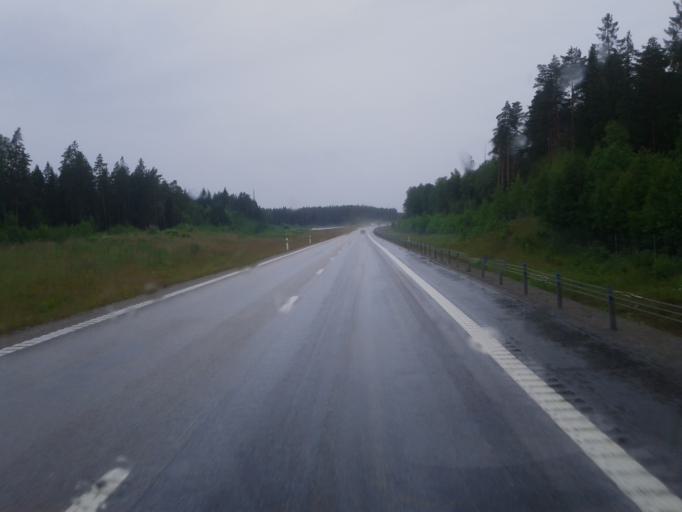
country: SE
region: Uppsala
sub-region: Tierps Kommun
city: Tierp
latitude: 60.2720
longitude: 17.5018
